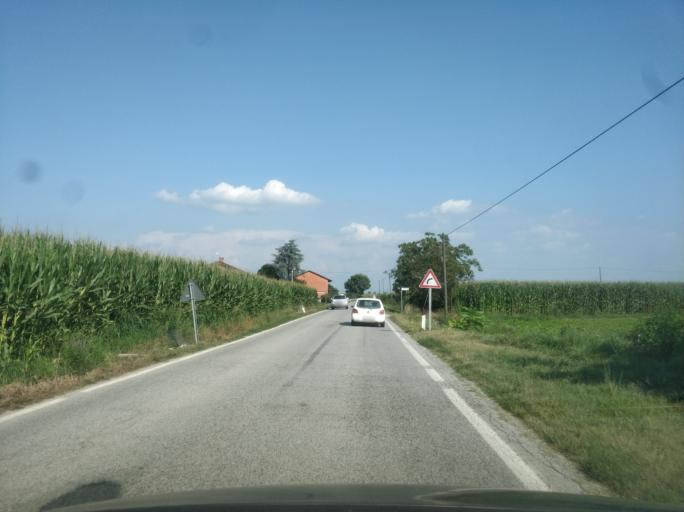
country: IT
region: Piedmont
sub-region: Provincia di Cuneo
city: Centallo
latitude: 44.5333
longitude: 7.6351
